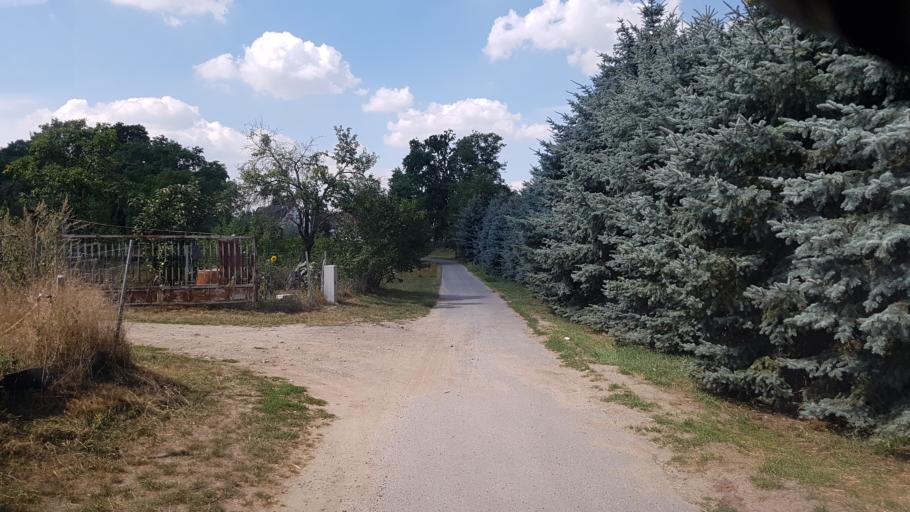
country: DE
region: Brandenburg
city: Hirschfeld
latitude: 51.3829
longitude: 13.6231
